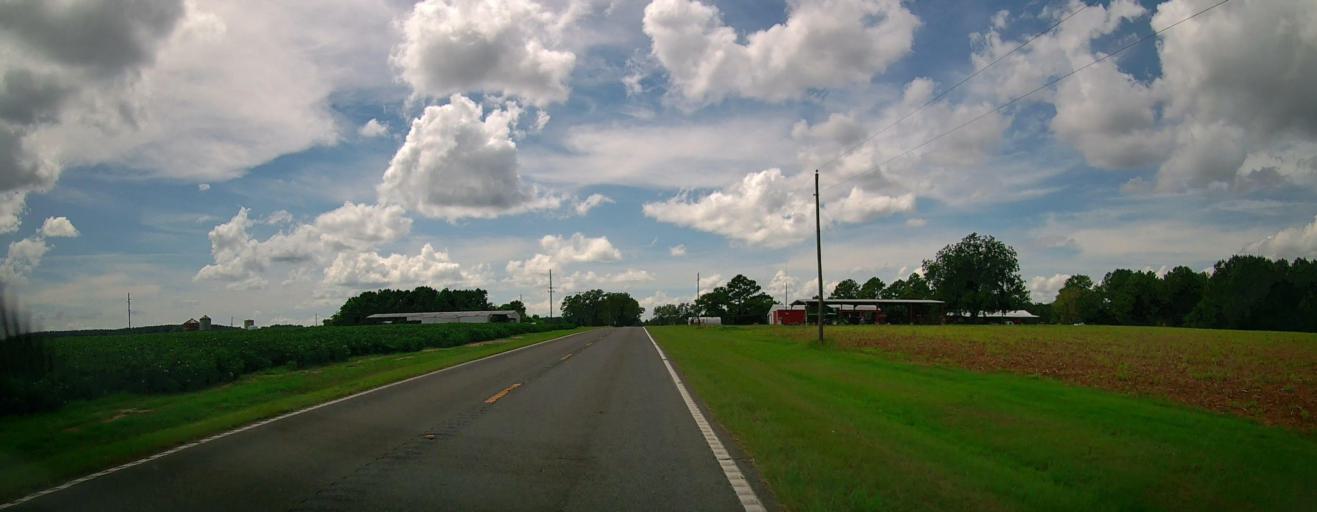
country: US
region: Georgia
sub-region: Taylor County
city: Reynolds
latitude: 32.4400
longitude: -84.0804
